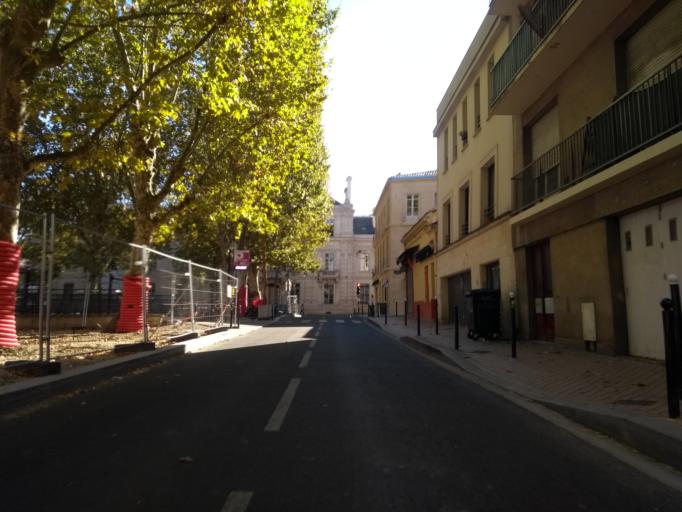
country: FR
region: Aquitaine
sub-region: Departement de la Gironde
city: Bordeaux
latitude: 44.8294
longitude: -0.5633
